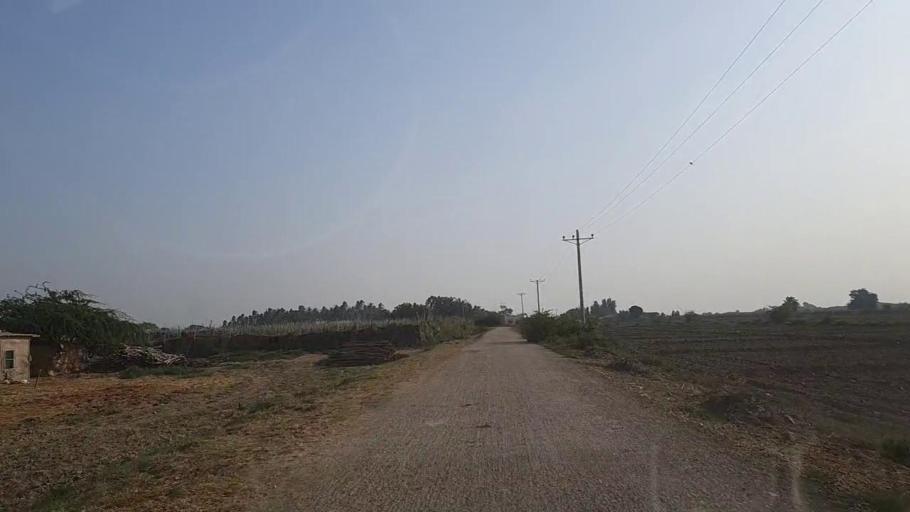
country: PK
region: Sindh
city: Keti Bandar
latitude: 24.1680
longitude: 67.6264
